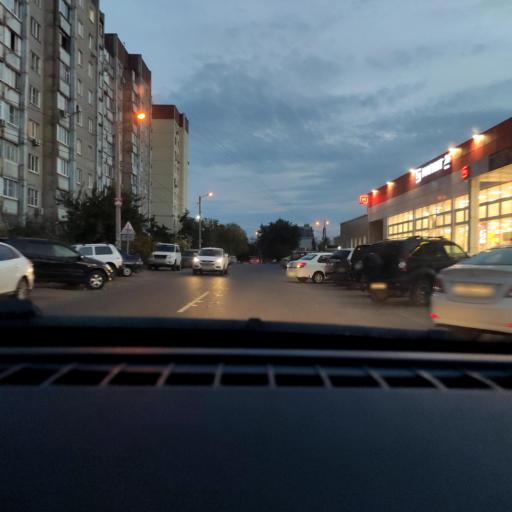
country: RU
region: Voronezj
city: Somovo
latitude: 51.7354
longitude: 39.2912
